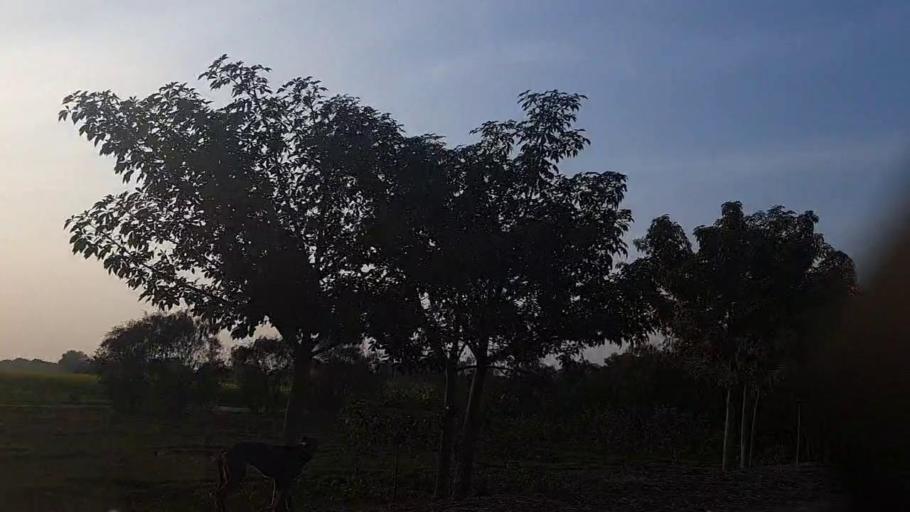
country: PK
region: Sindh
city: Sakrand
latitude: 26.1207
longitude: 68.2248
